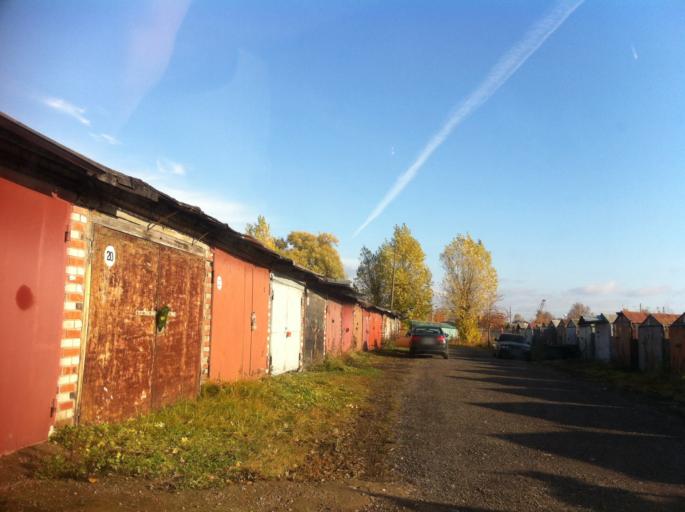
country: RU
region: St.-Petersburg
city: Uritsk
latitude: 59.8222
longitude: 30.1653
